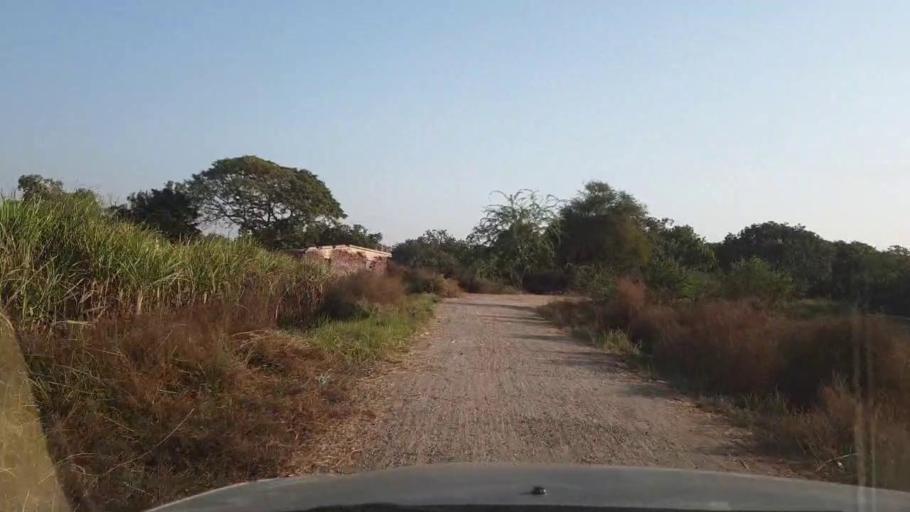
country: PK
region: Sindh
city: Tando Muhammad Khan
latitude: 25.1234
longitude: 68.5524
